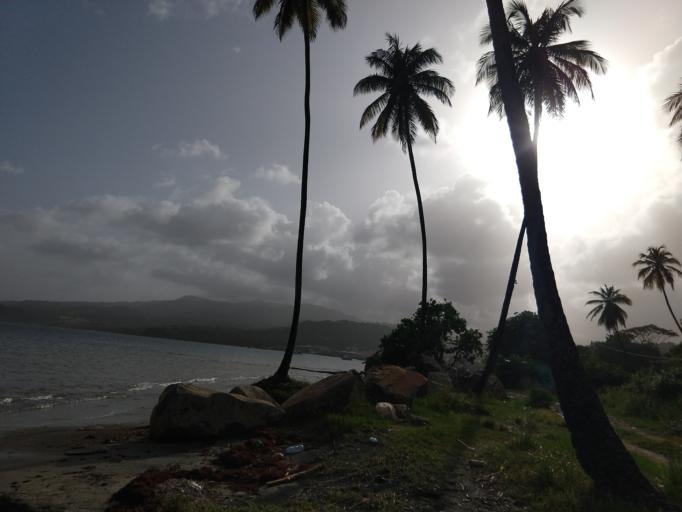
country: GD
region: Saint Andrew
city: Grenville
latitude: 12.1247
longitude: -61.6164
